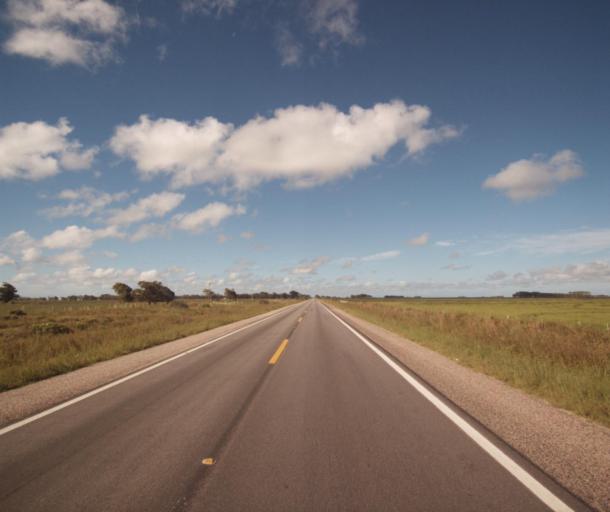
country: UY
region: Cerro Largo
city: Rio Branco
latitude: -32.9535
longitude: -52.7787
